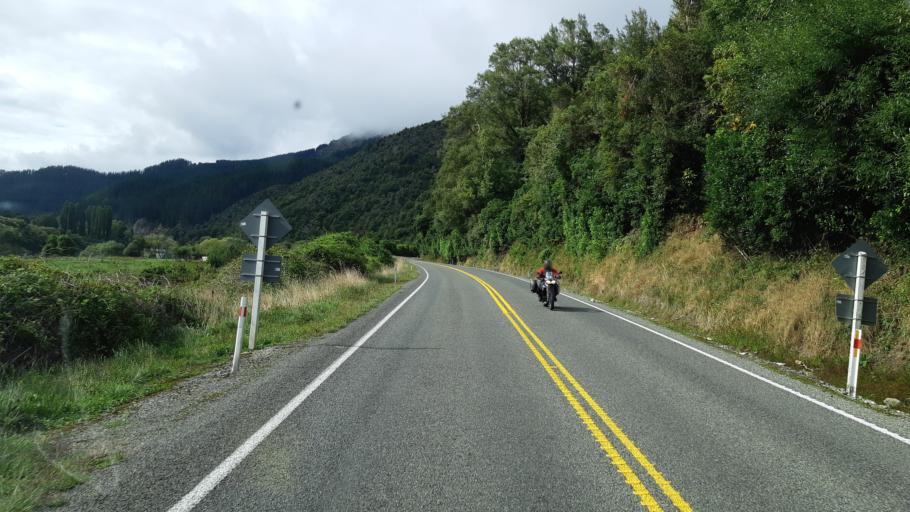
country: NZ
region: West Coast
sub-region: Buller District
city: Westport
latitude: -41.7703
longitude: 172.2365
